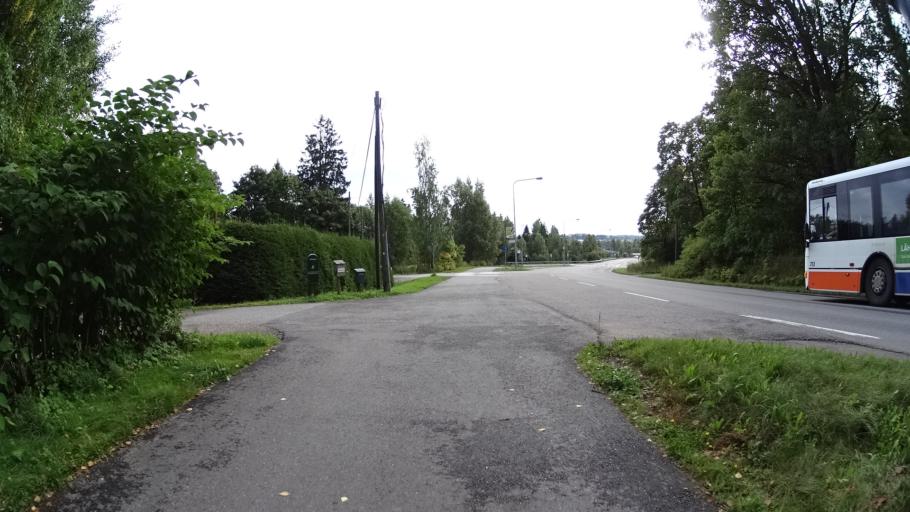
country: FI
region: Uusimaa
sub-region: Helsinki
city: Espoo
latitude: 60.2254
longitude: 24.6700
